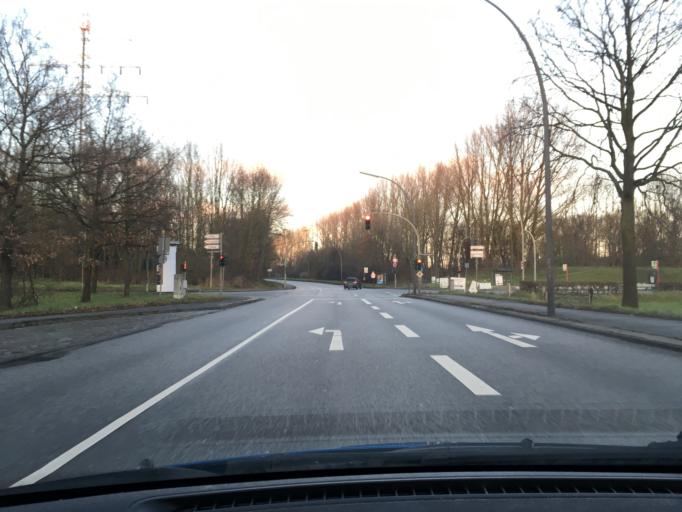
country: DE
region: Hamburg
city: Altona
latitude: 53.4950
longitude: 9.9100
